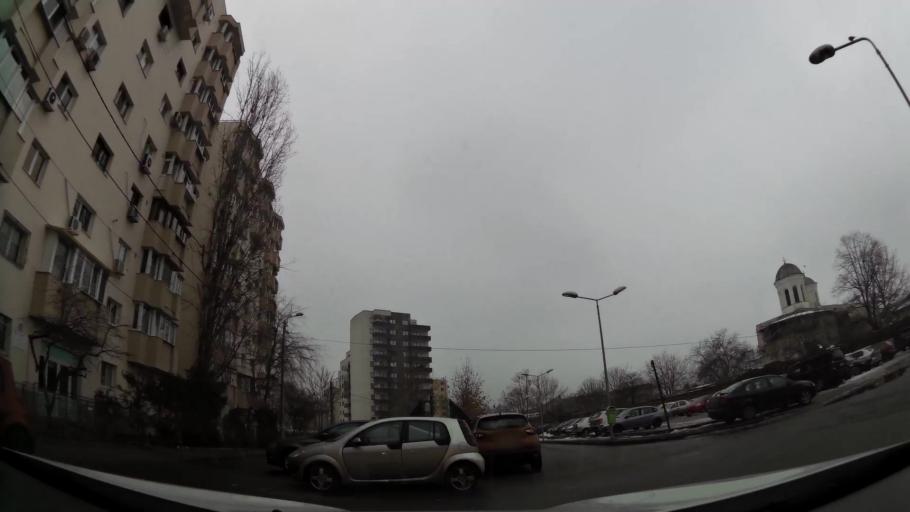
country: RO
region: Bucuresti
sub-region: Municipiul Bucuresti
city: Bucharest
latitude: 44.4151
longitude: 26.1241
